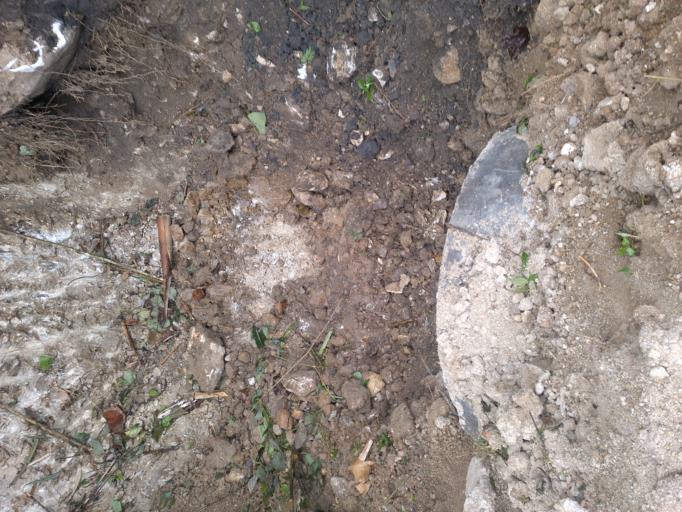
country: LA
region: Houaphan
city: Xamtay
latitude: 19.8233
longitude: 104.4813
